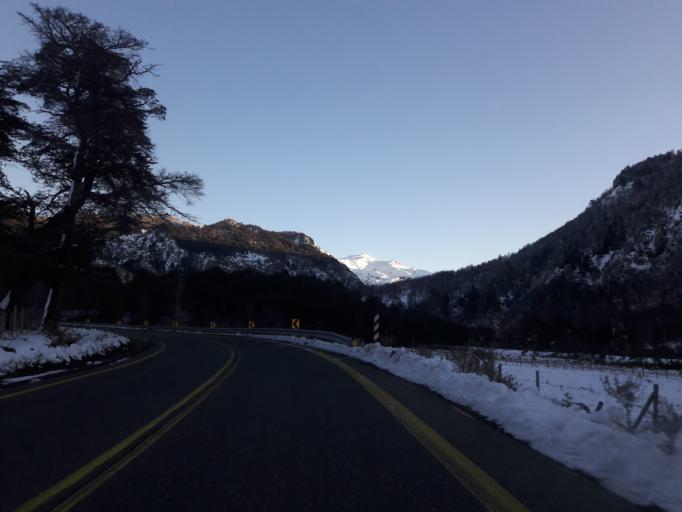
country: CL
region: Araucania
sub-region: Provincia de Cautin
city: Vilcun
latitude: -38.5013
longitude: -71.5201
